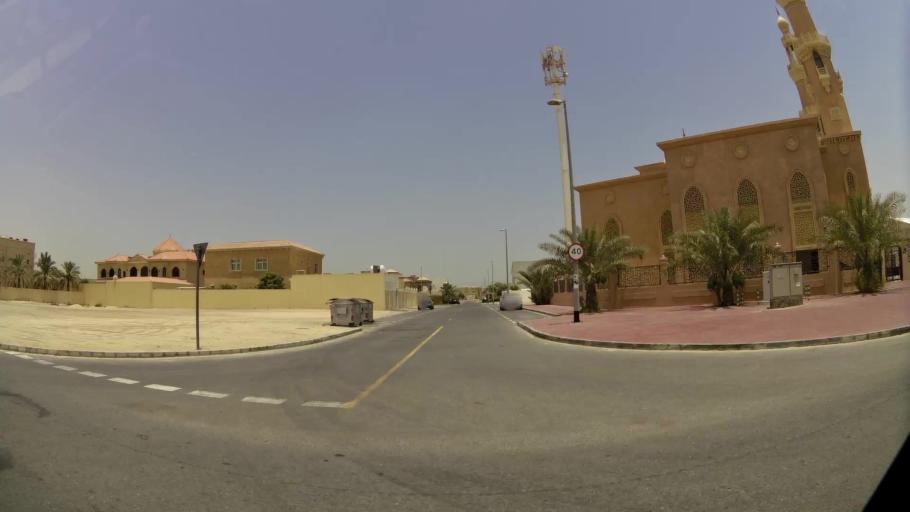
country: AE
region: Dubai
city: Dubai
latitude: 25.0924
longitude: 55.2356
